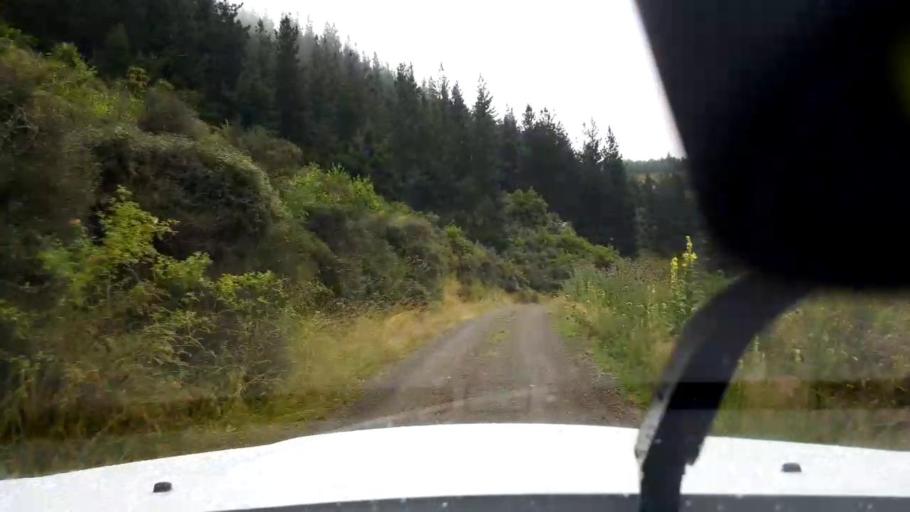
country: NZ
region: Canterbury
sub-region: Timaru District
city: Pleasant Point
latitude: -44.0336
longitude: 170.9952
